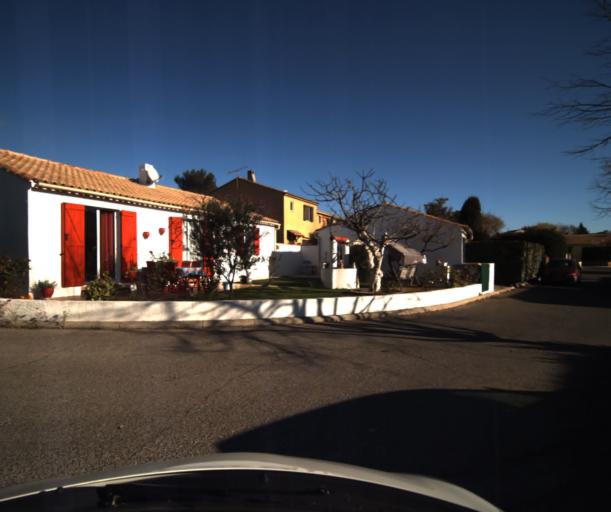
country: FR
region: Provence-Alpes-Cote d'Azur
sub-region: Departement du Vaucluse
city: Pertuis
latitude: 43.7006
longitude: 5.5077
